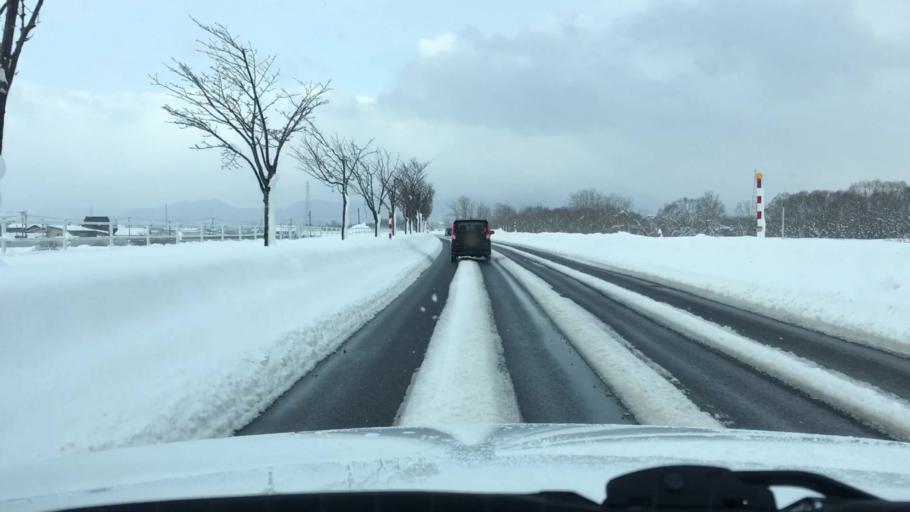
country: JP
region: Aomori
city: Hirosaki
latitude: 40.6364
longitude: 140.4717
